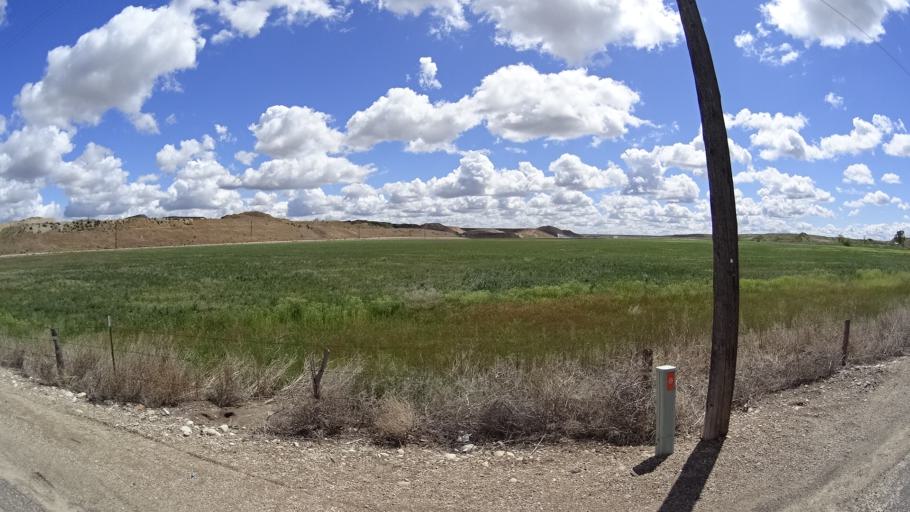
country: US
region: Idaho
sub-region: Ada County
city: Garden City
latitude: 43.4913
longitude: -116.2745
